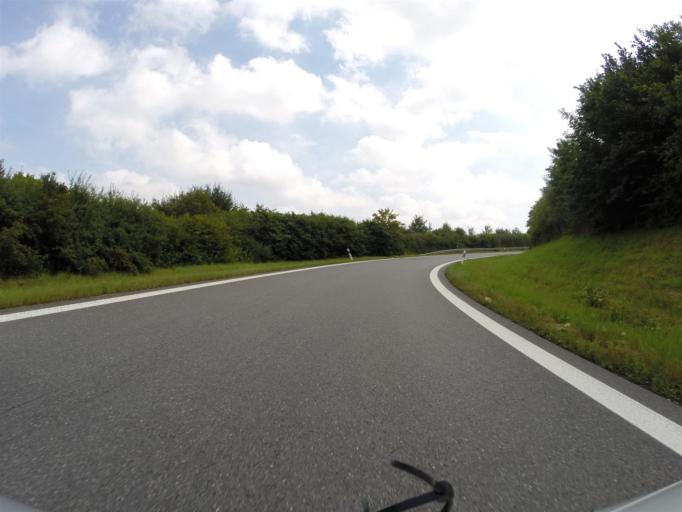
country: DE
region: North Rhine-Westphalia
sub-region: Regierungsbezirk Detmold
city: Herford
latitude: 52.0893
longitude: 8.6976
